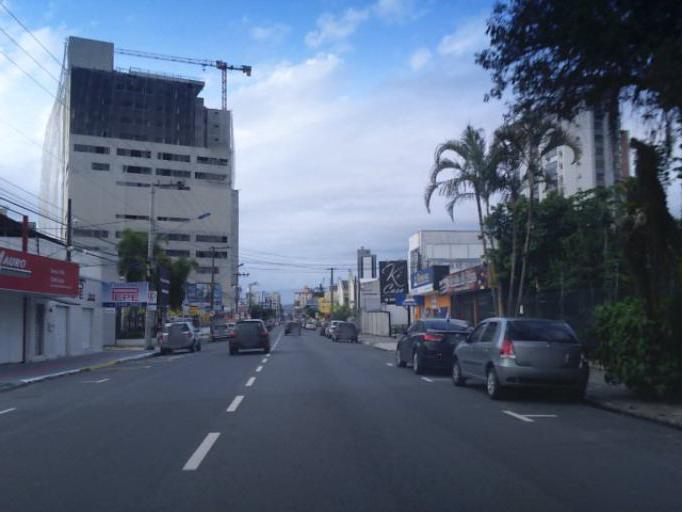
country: BR
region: Santa Catarina
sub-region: Itajai
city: Itajai
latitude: -26.9112
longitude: -48.6574
